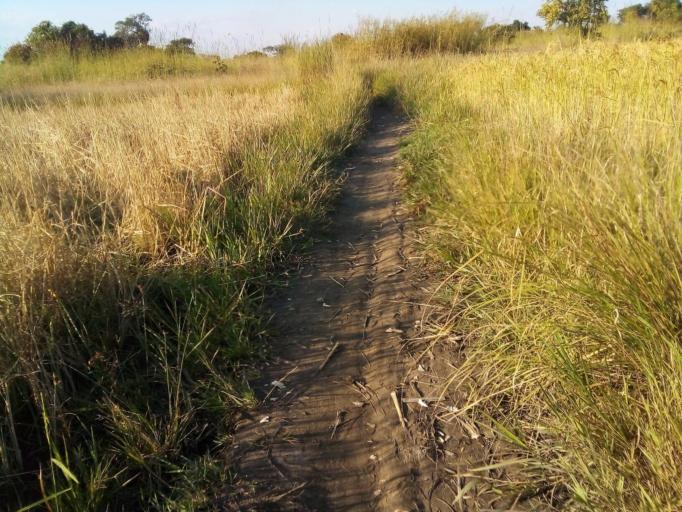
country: MZ
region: Zambezia
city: Quelimane
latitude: -17.4810
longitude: 36.8168
